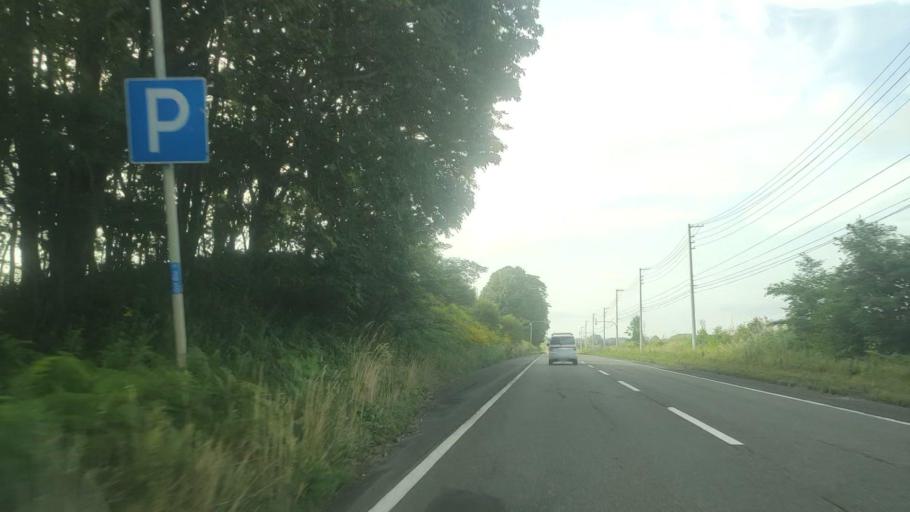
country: JP
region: Hokkaido
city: Chitose
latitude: 42.9011
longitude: 141.8134
